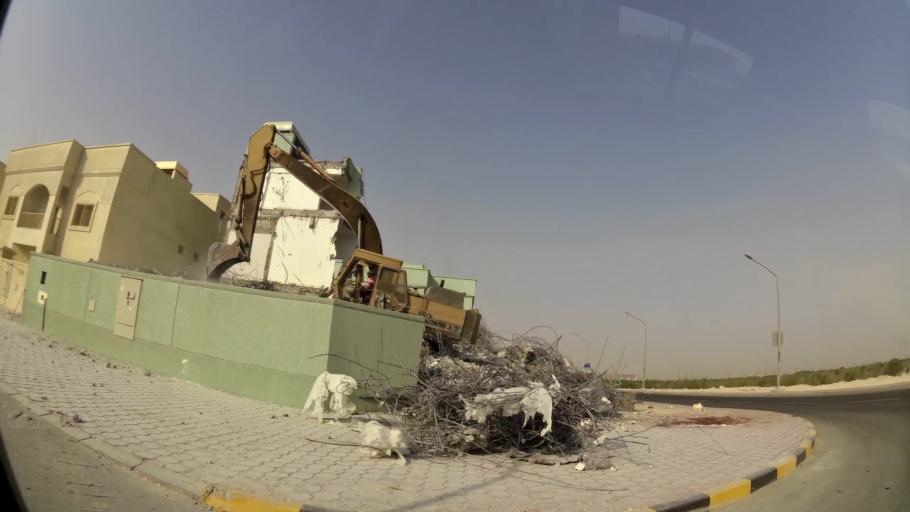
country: KW
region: Al Asimah
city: Ar Rabiyah
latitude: 29.3347
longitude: 47.8083
